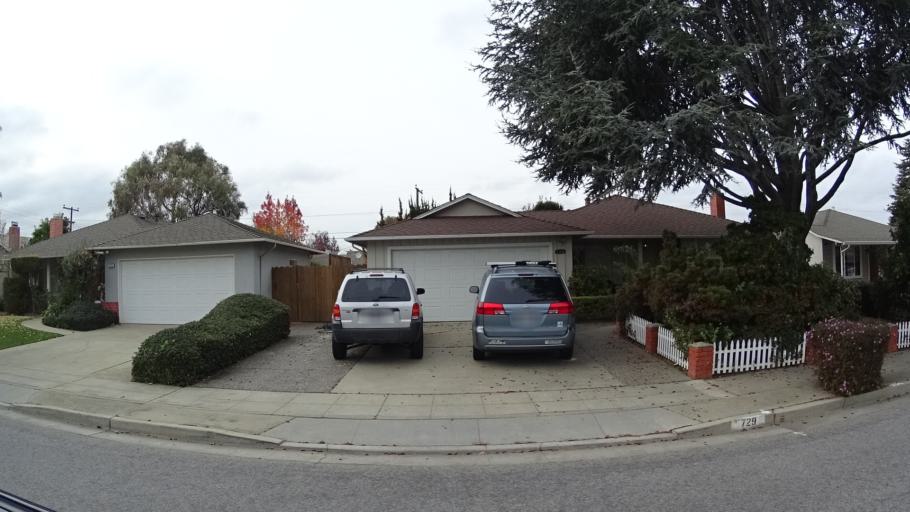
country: US
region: California
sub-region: Santa Clara County
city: Sunnyvale
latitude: 37.3695
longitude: -122.0485
